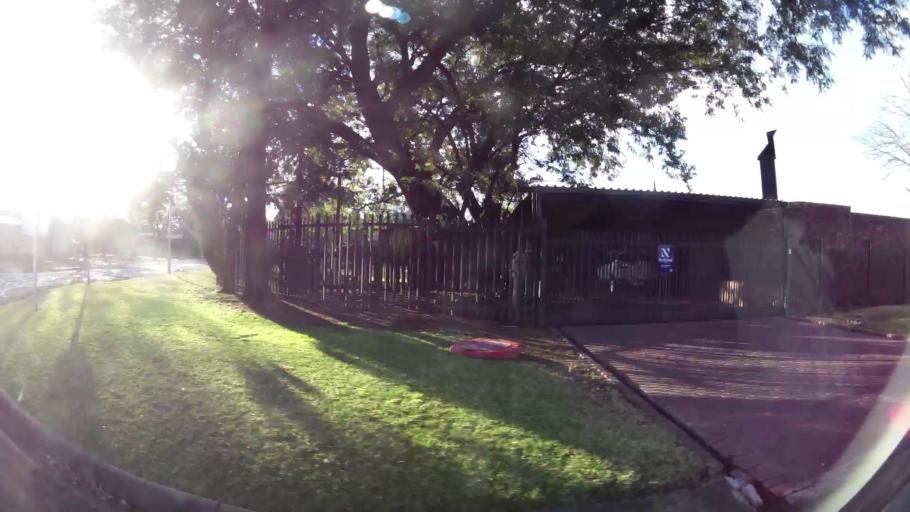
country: ZA
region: Orange Free State
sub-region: Mangaung Metropolitan Municipality
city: Bloemfontein
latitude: -29.1469
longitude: 26.1835
